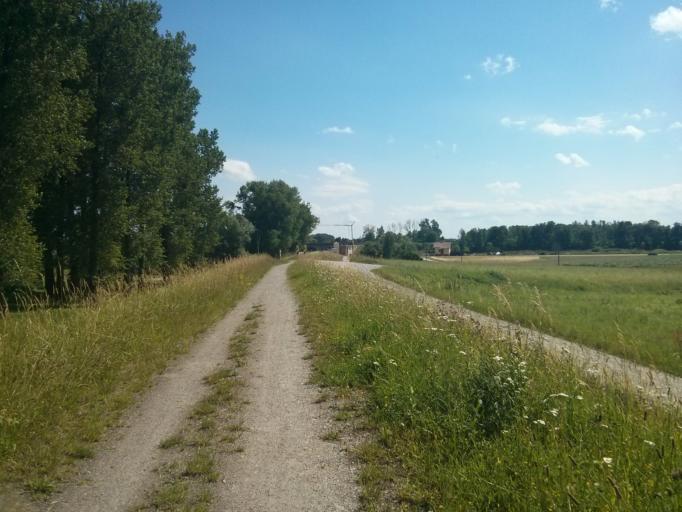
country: DE
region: Bavaria
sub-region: Lower Bavaria
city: Deggendorf
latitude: 48.8167
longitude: 12.9642
